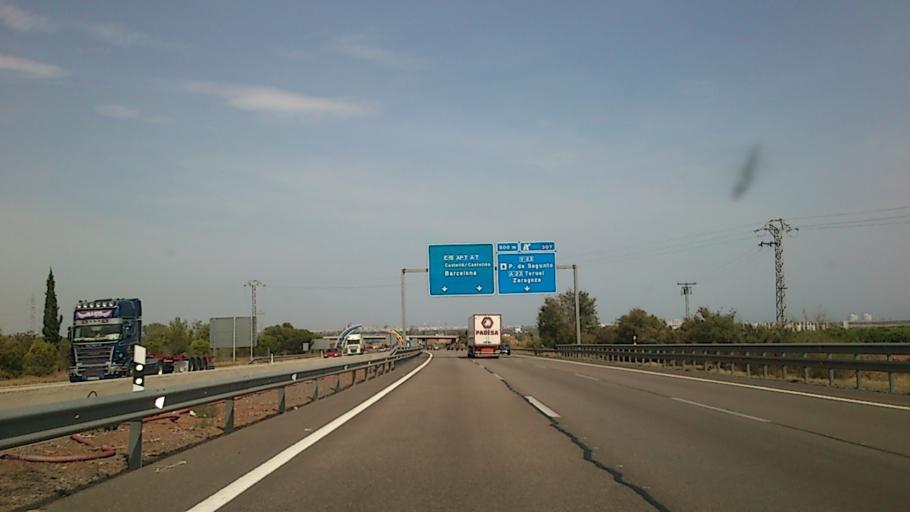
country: ES
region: Valencia
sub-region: Provincia de Valencia
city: Pucol
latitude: 39.6274
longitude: -0.3147
